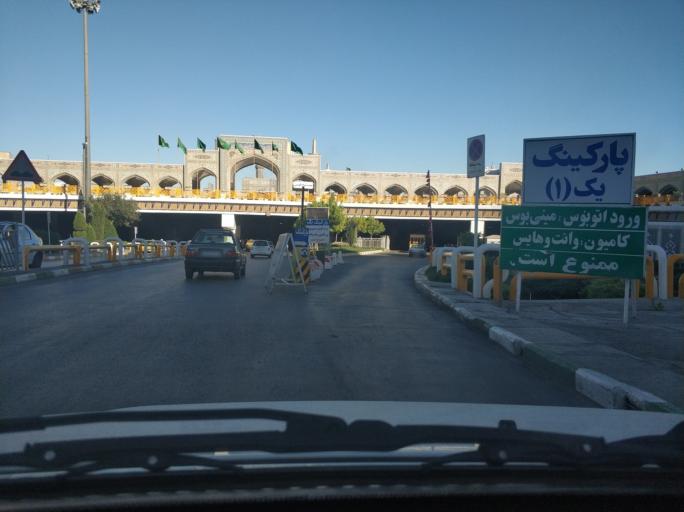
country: IR
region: Razavi Khorasan
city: Mashhad
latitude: 36.2910
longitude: 59.6134
